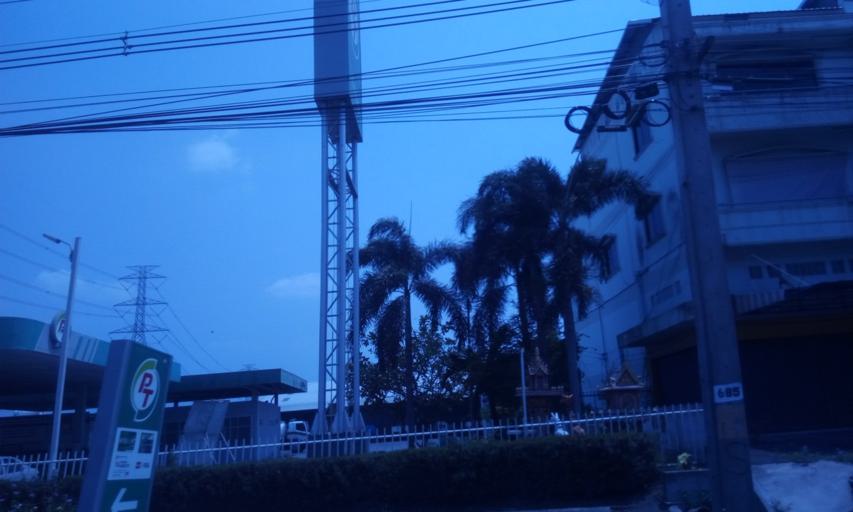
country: TH
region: Chachoengsao
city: Bang Nam Priao
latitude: 13.8250
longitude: 101.0544
